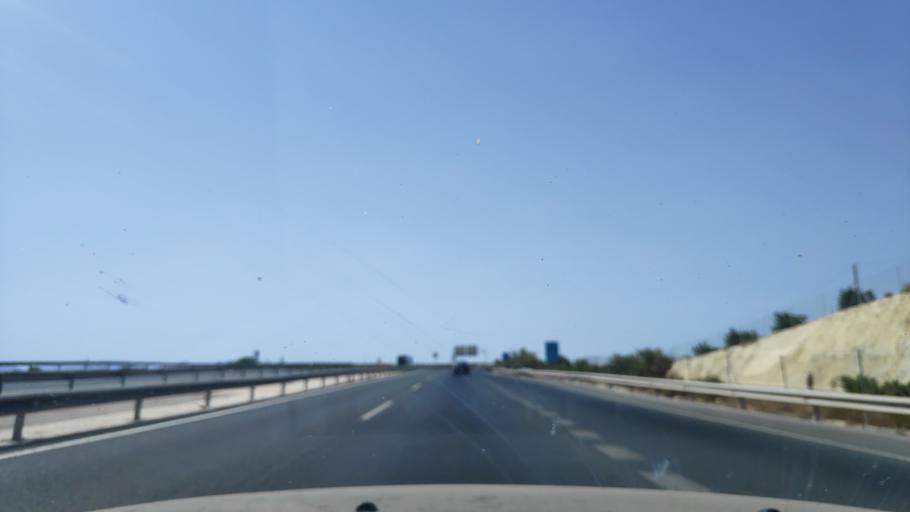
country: ES
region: Murcia
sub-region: Murcia
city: Lorqui
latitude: 38.1049
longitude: -1.2361
